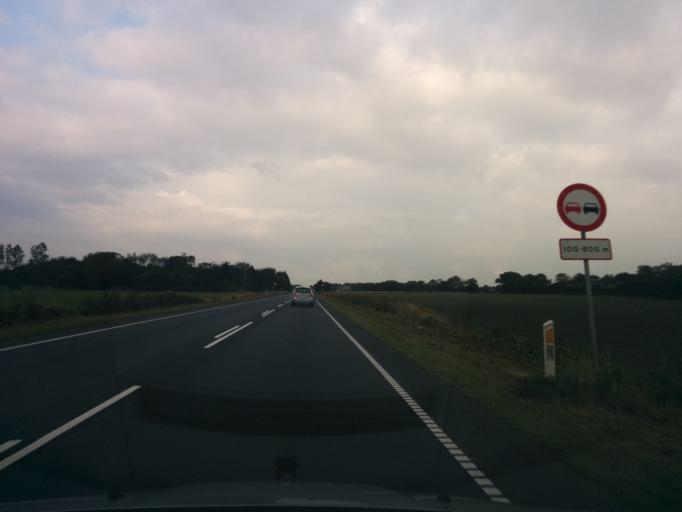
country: DK
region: South Denmark
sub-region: Esbjerg Kommune
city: Bramming
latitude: 55.6134
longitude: 8.7485
